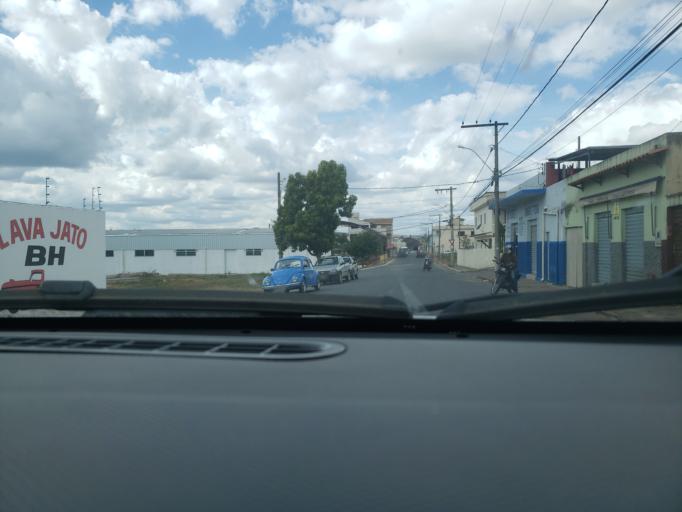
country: BR
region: Minas Gerais
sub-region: Campo Belo
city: Campo Belo
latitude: -20.9048
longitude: -45.2796
